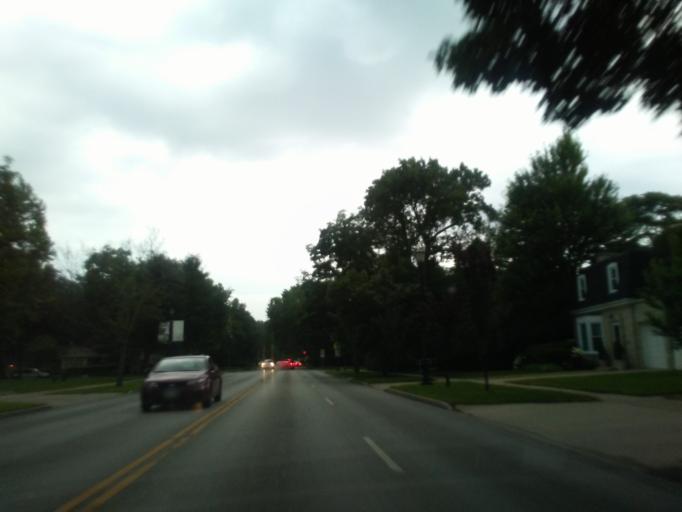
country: US
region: Illinois
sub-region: Cook County
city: Evanston
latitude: 42.0285
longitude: -87.6857
